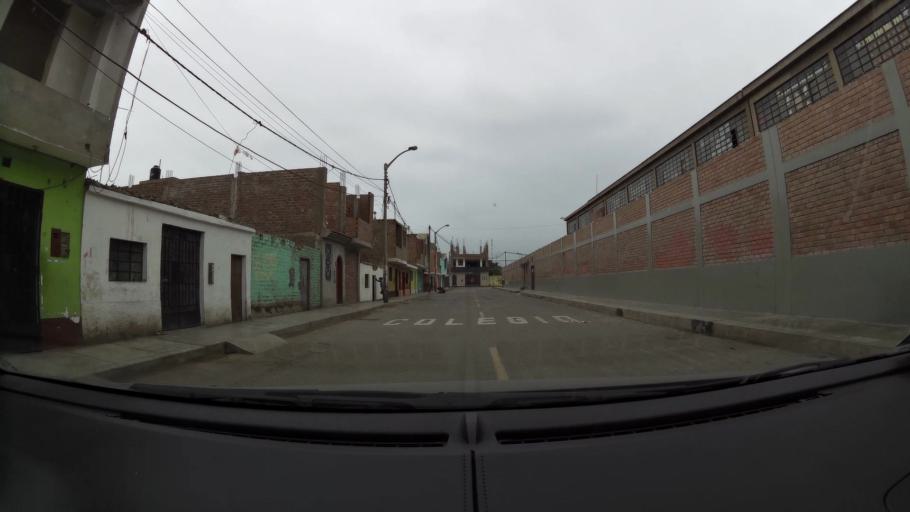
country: PE
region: Lima
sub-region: Barranca
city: Barranca
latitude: -10.7462
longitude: -77.7522
